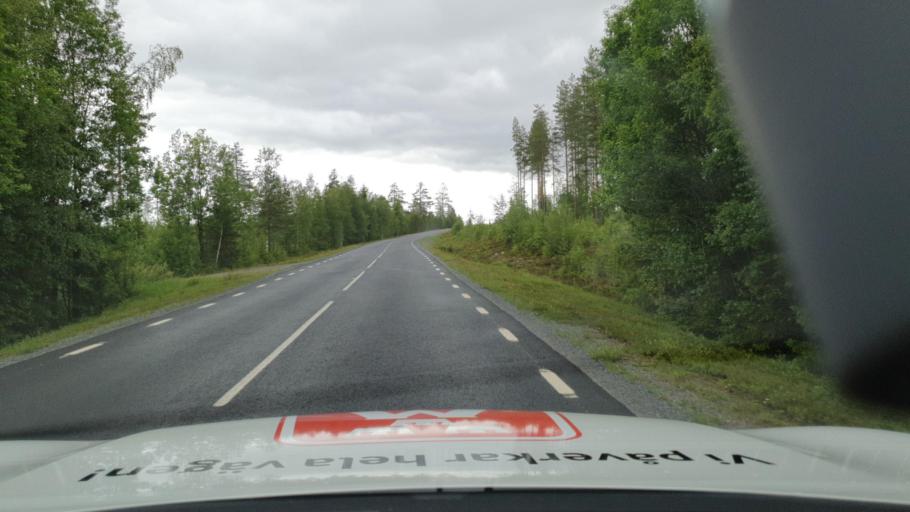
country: SE
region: Vaesterbotten
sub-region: Dorotea Kommun
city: Dorotea
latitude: 64.2032
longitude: 16.5659
